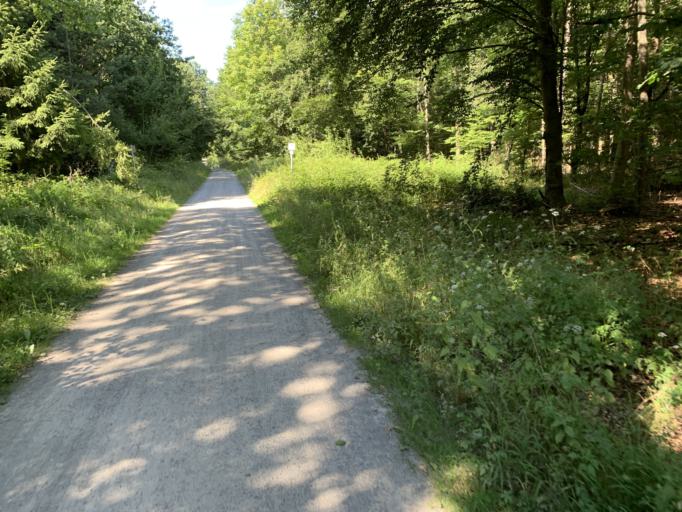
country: DE
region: Baden-Wuerttemberg
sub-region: Karlsruhe Region
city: Tiefenbronn
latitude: 48.8351
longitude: 8.7990
